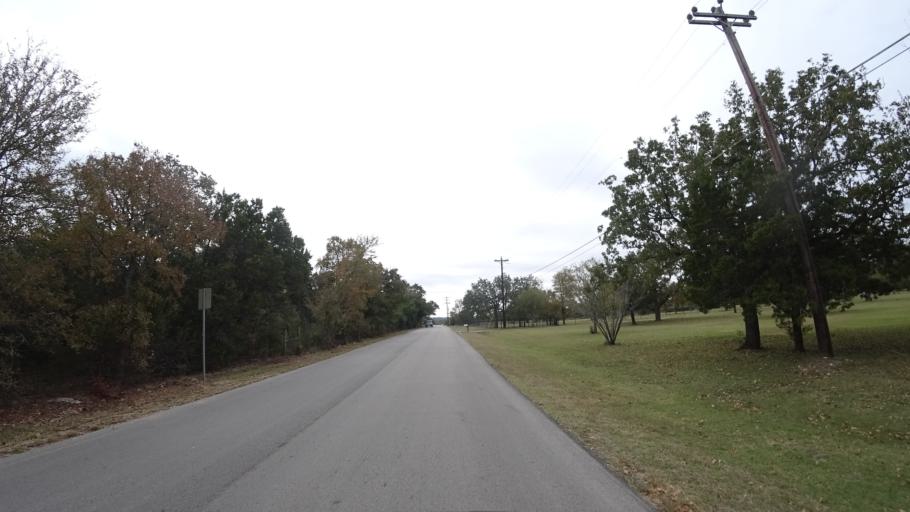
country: US
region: Texas
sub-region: Travis County
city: Shady Hollow
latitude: 30.1439
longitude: -97.8743
